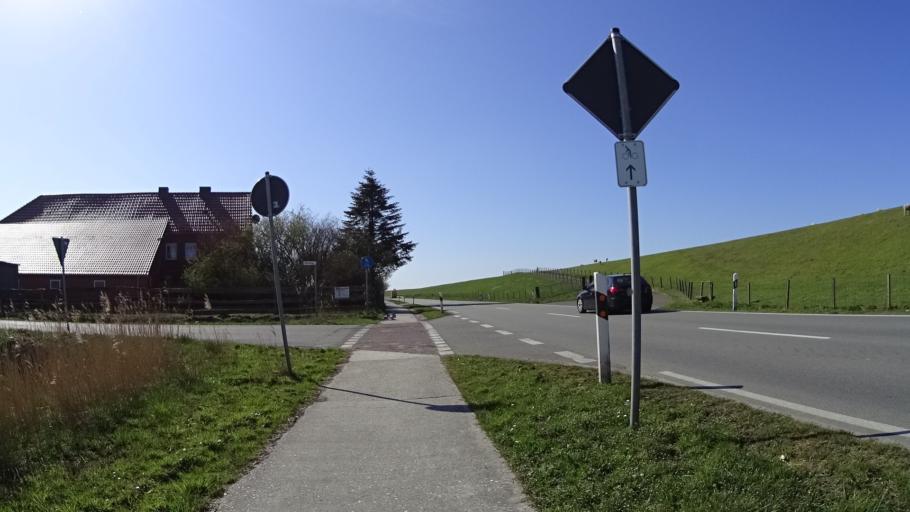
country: DE
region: Lower Saxony
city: Jemgum
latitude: 53.2419
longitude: 7.4073
